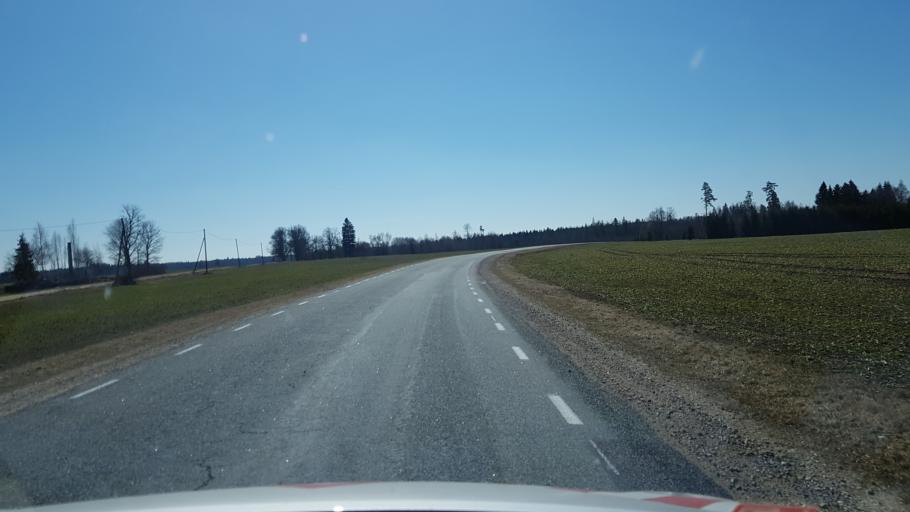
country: EE
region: Laeaene-Virumaa
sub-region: Rakke vald
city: Rakke
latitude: 59.0225
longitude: 26.3532
